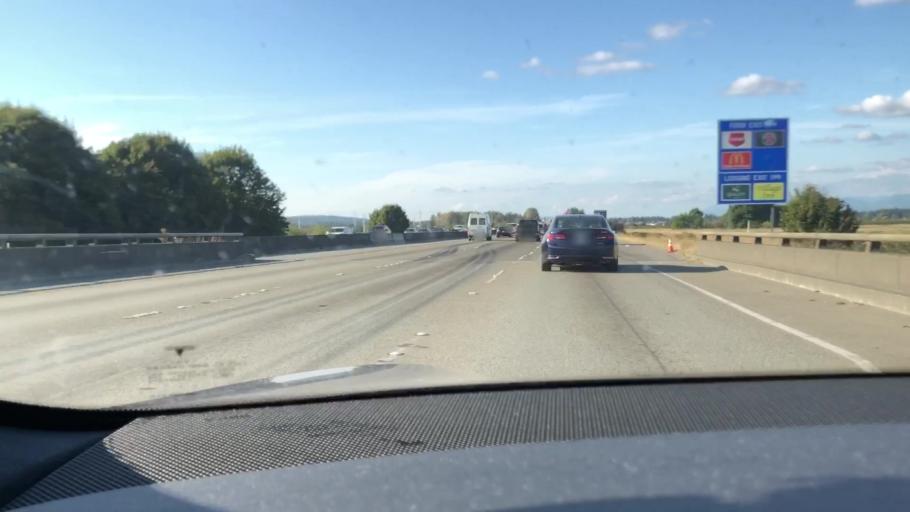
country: US
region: Washington
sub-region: Snohomish County
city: Marysville
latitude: 48.0229
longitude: -122.1786
